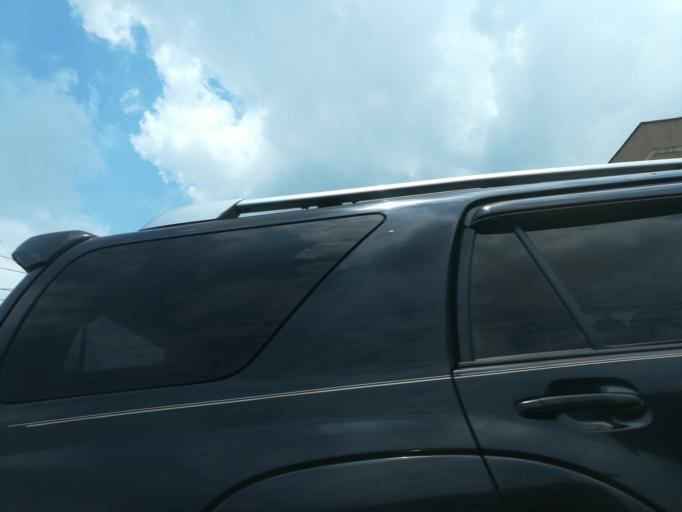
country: NG
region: Lagos
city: Oshodi
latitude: 6.5455
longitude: 3.3329
